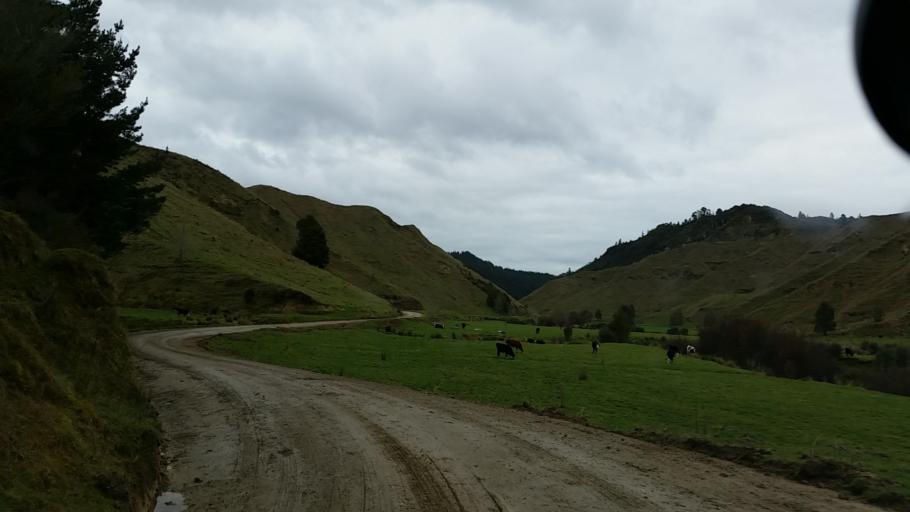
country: NZ
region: Taranaki
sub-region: South Taranaki District
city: Patea
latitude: -39.6663
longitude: 174.7480
